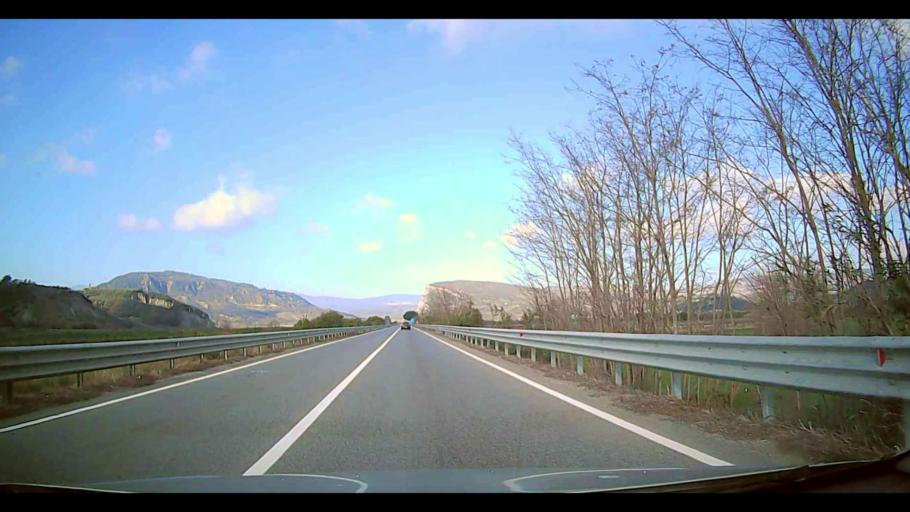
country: IT
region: Calabria
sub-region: Provincia di Crotone
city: Santa Severina
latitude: 39.1768
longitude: 16.9289
